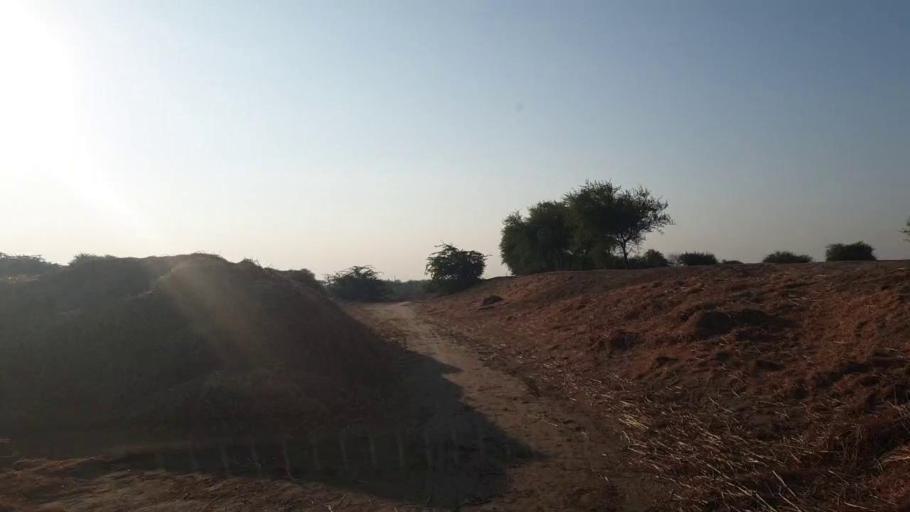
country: PK
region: Sindh
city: Badin
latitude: 24.6357
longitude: 68.7938
